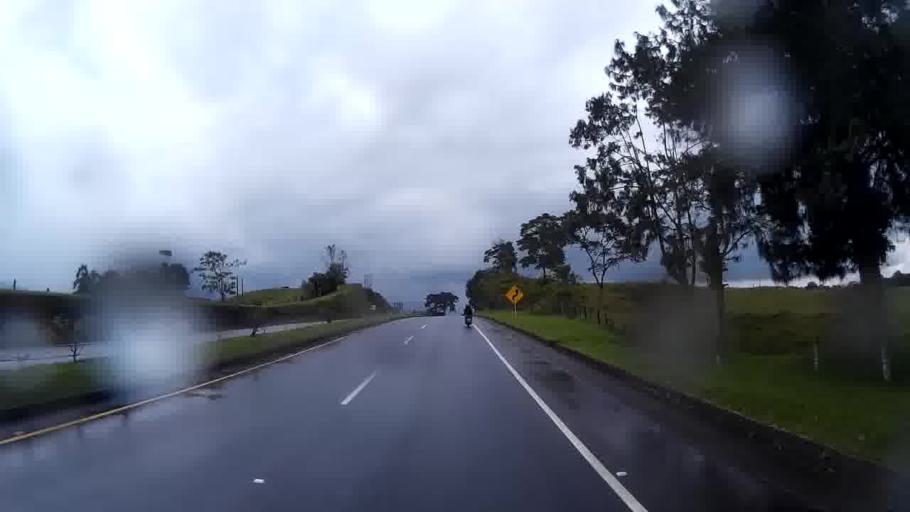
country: CO
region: Quindio
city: Salento
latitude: 4.6697
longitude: -75.5961
